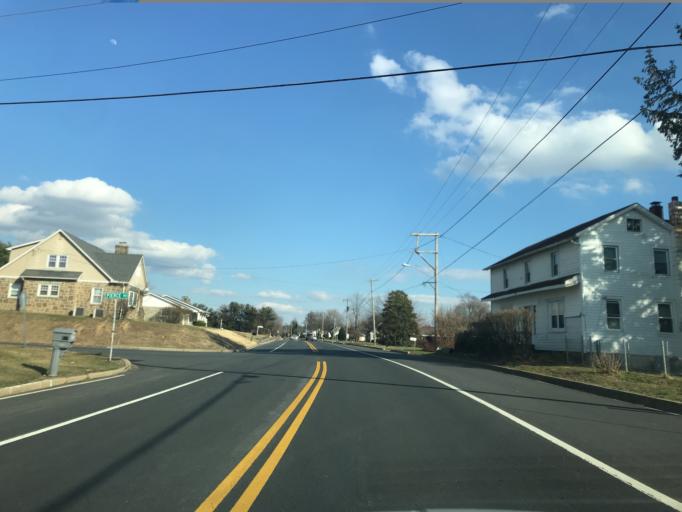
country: US
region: Maryland
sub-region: Cecil County
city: Rising Sun
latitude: 39.6912
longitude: -76.0491
